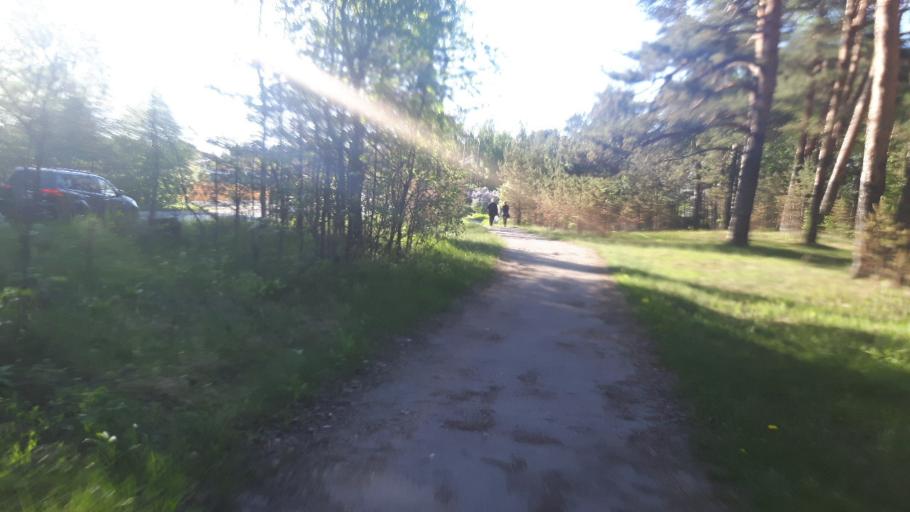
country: RU
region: St.-Petersburg
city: Bol'shaya Izhora
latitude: 59.9429
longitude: 29.5779
